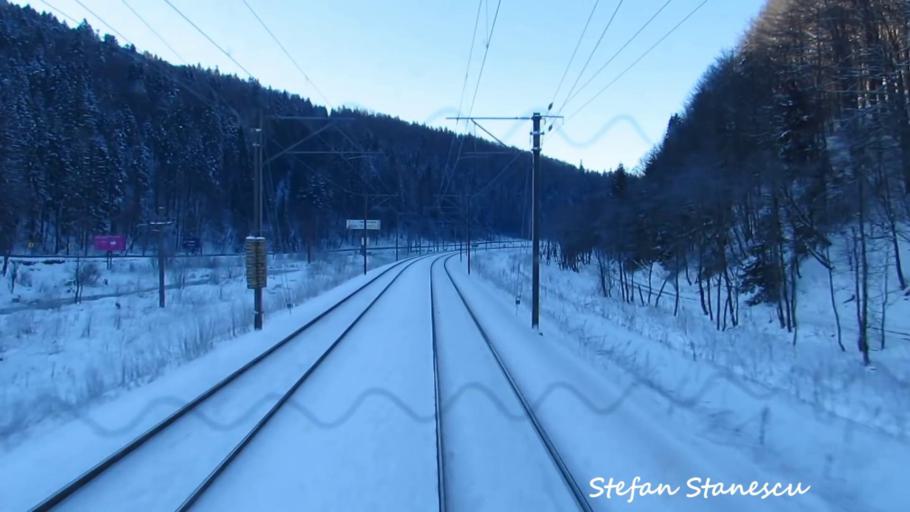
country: RO
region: Prahova
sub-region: Oras Azuga
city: Azuga
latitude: 45.4591
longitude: 25.5658
